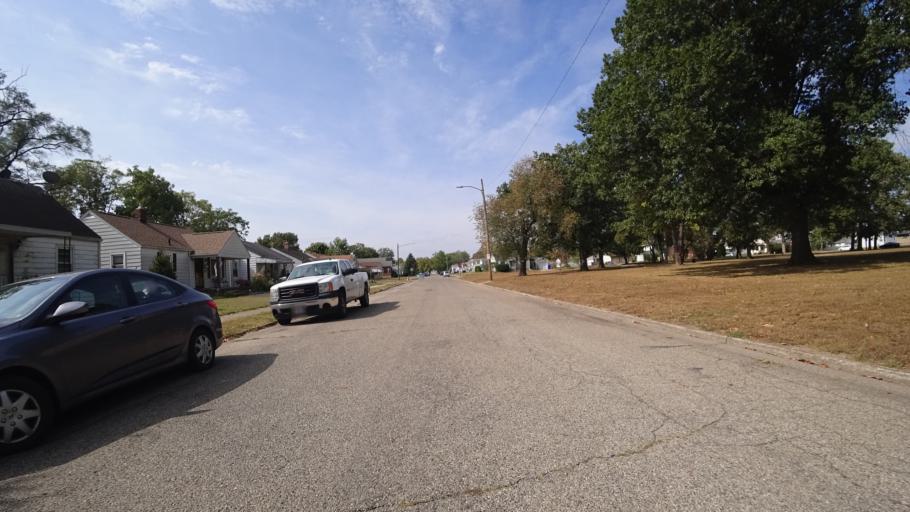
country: US
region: Ohio
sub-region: Butler County
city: Fairfield
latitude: 39.3601
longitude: -84.5522
